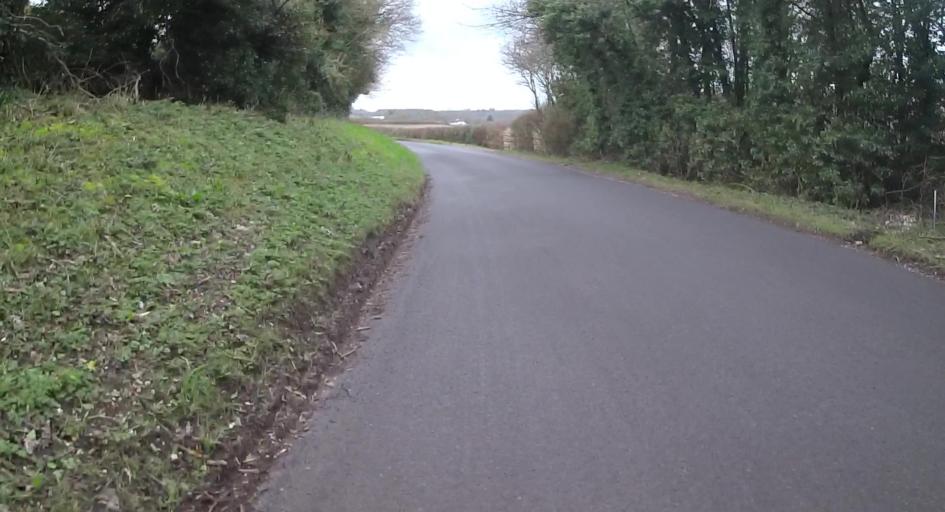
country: GB
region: England
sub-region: Hampshire
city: Kingsclere
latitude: 51.3279
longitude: -1.2686
